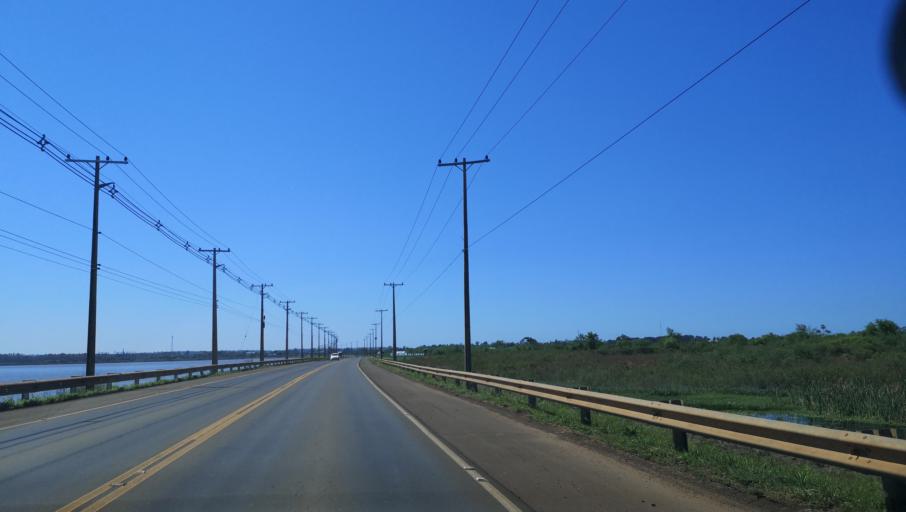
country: PY
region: Itapua
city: Carmen del Parana
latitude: -27.2089
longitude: -56.1619
